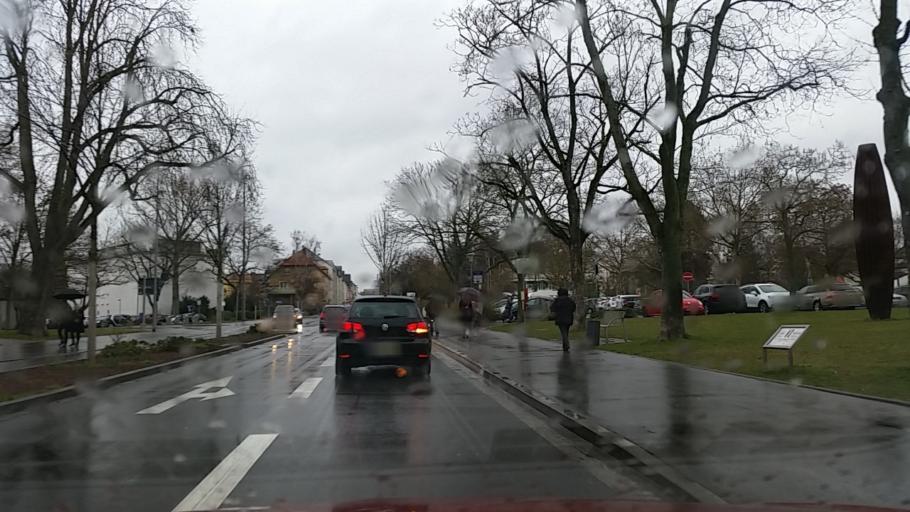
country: DE
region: Bavaria
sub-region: Regierungsbezirk Unterfranken
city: Schweinfurt
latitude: 50.0439
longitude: 10.2261
